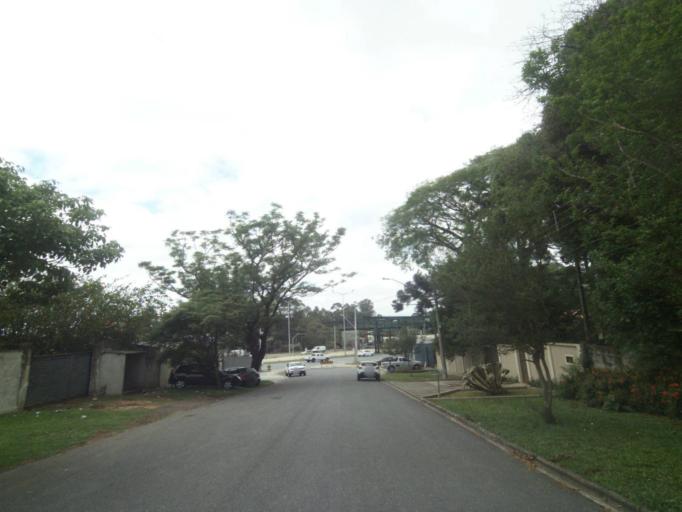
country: BR
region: Parana
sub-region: Pinhais
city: Pinhais
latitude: -25.4190
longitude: -49.2252
